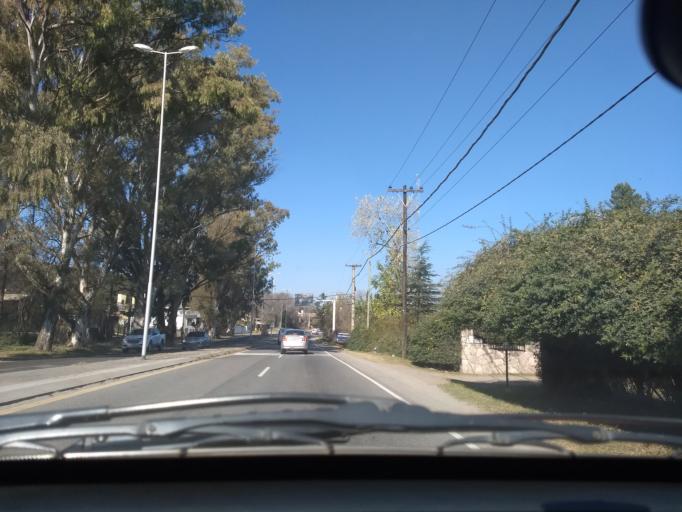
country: AR
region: Cordoba
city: Rio Ceballos
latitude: -31.1722
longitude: -64.3024
